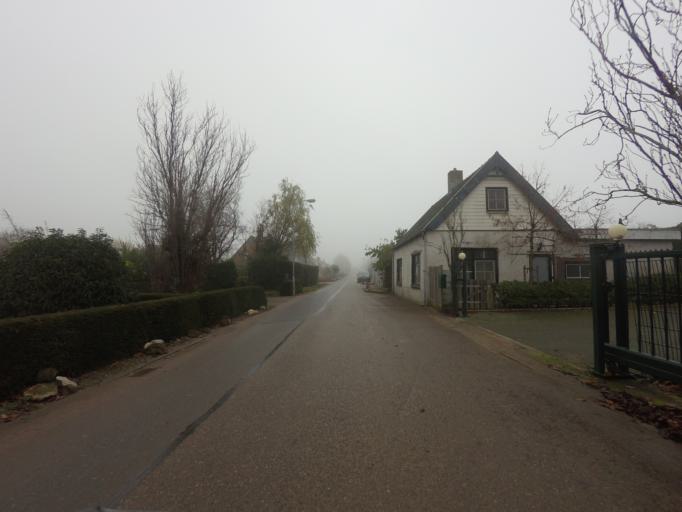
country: NL
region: Gelderland
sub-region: Gemeente Zaltbommel
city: Nederhemert
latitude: 51.7624
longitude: 5.1558
